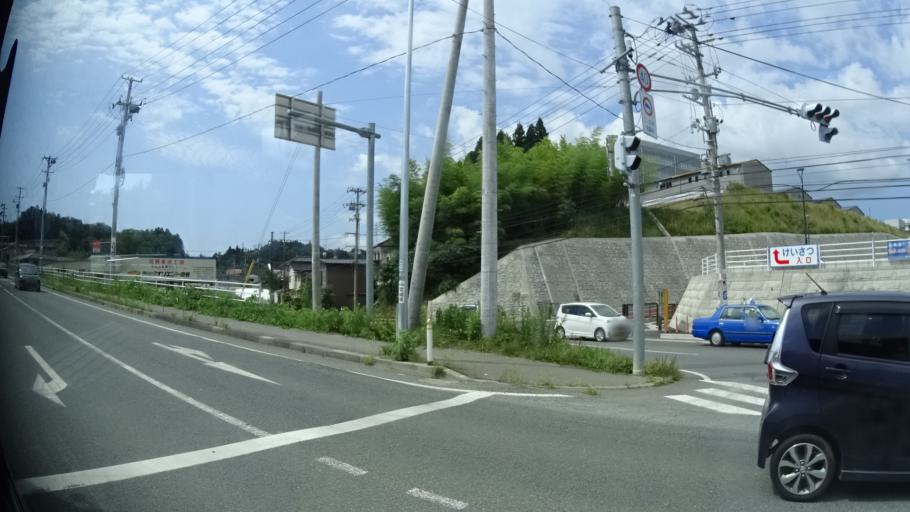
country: JP
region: Iwate
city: Ofunato
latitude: 38.8882
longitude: 141.5712
